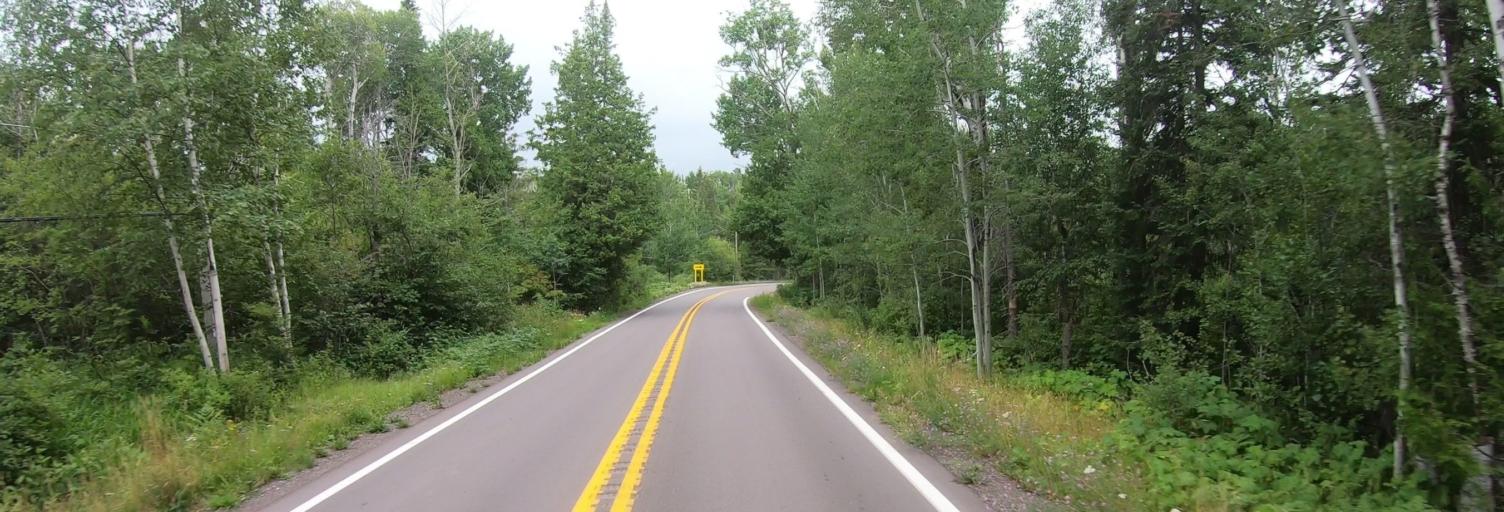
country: US
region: Michigan
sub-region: Keweenaw County
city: Eagle River
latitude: 47.4653
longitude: -88.0675
